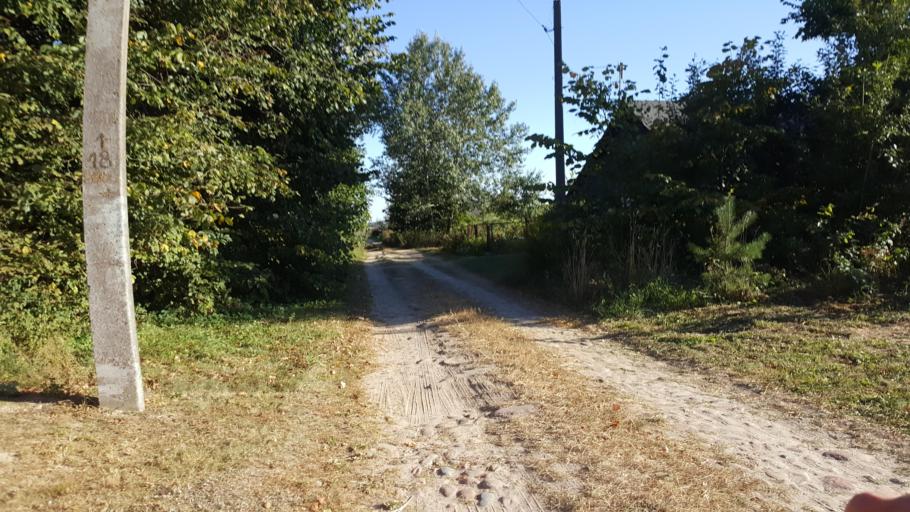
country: BY
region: Brest
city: Vysokaye
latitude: 52.3331
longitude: 23.2973
